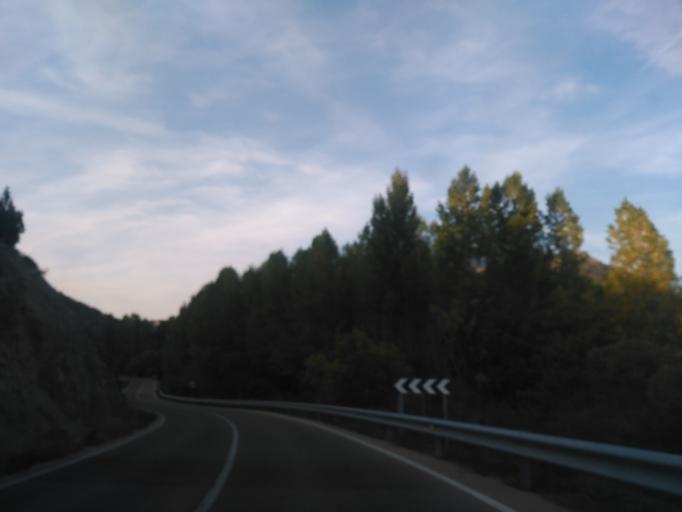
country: ES
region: Castille and Leon
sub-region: Provincia de Soria
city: Ucero
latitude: 41.7224
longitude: -3.0467
